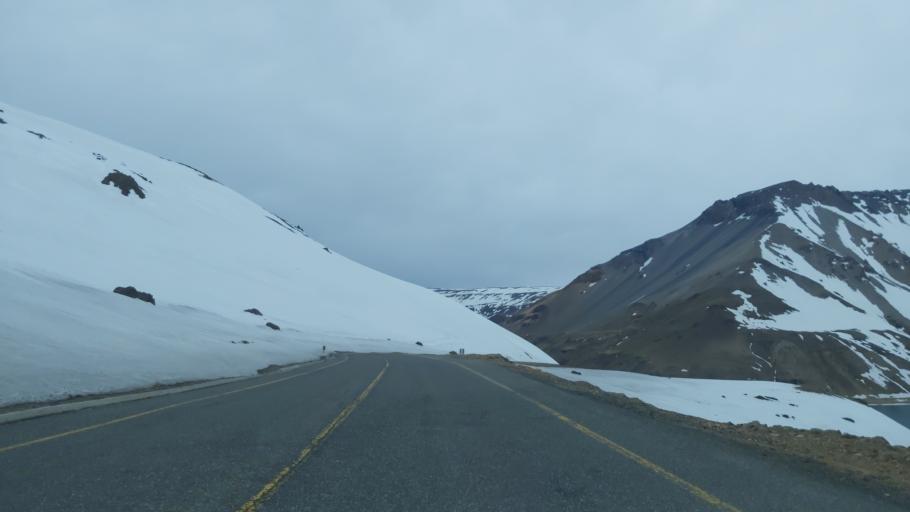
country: CL
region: Maule
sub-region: Provincia de Linares
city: Colbun
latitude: -36.0064
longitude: -70.4733
